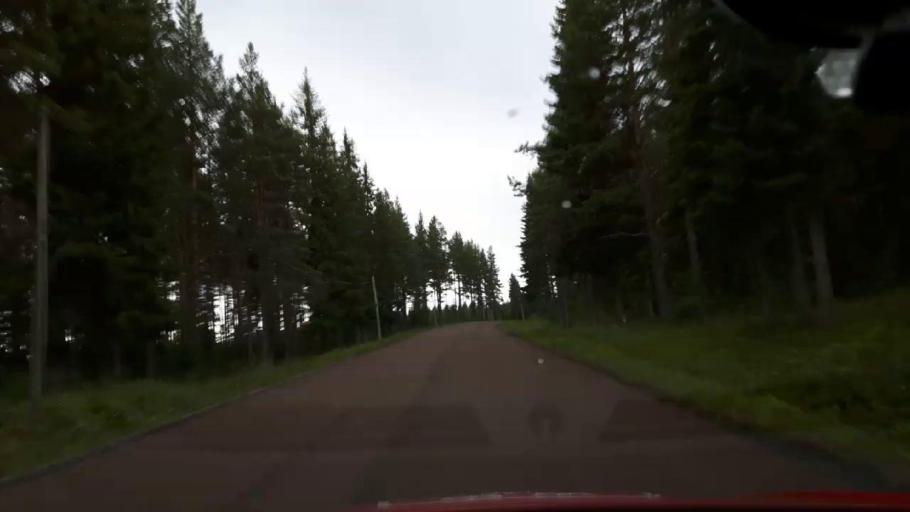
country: SE
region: Jaemtland
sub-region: Are Kommun
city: Jarpen
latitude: 63.3186
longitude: 13.6945
